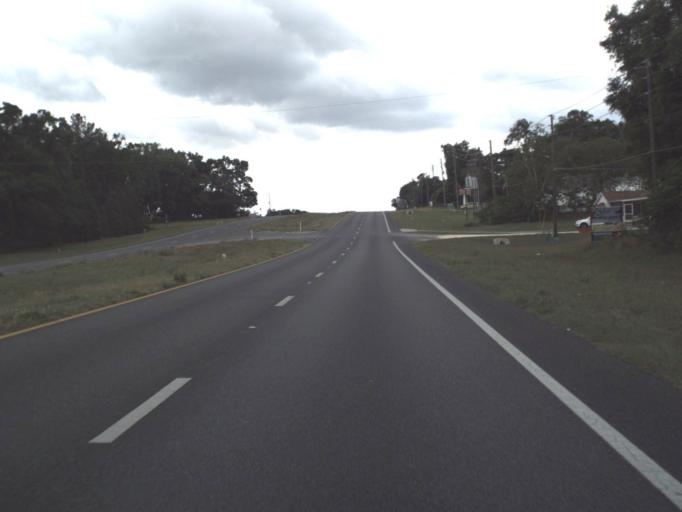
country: US
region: Florida
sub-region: Marion County
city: Belleview
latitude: 29.0465
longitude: -82.0460
